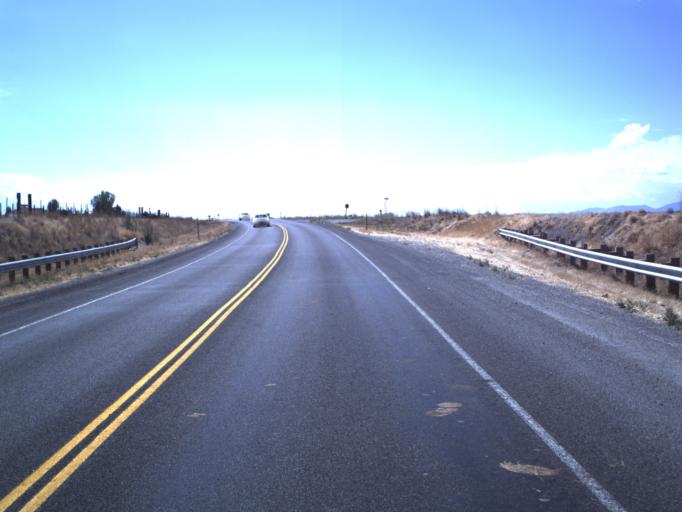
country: US
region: Utah
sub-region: Box Elder County
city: Honeyville
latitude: 41.5930
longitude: -112.1292
